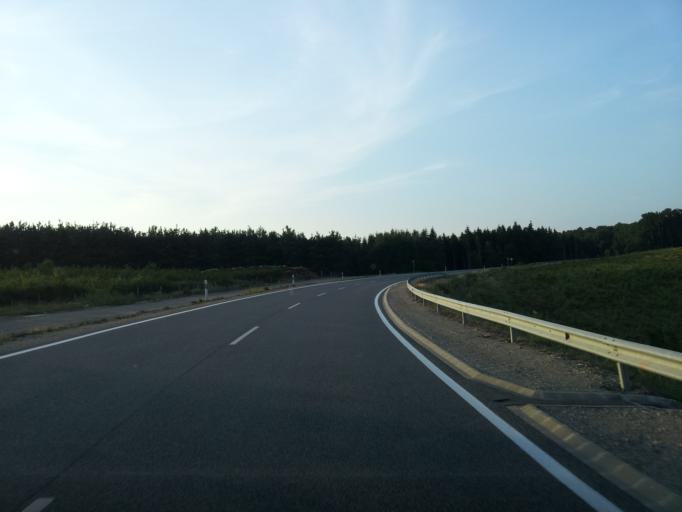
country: HU
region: Zala
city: Zalalovo
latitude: 46.7826
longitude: 16.5660
